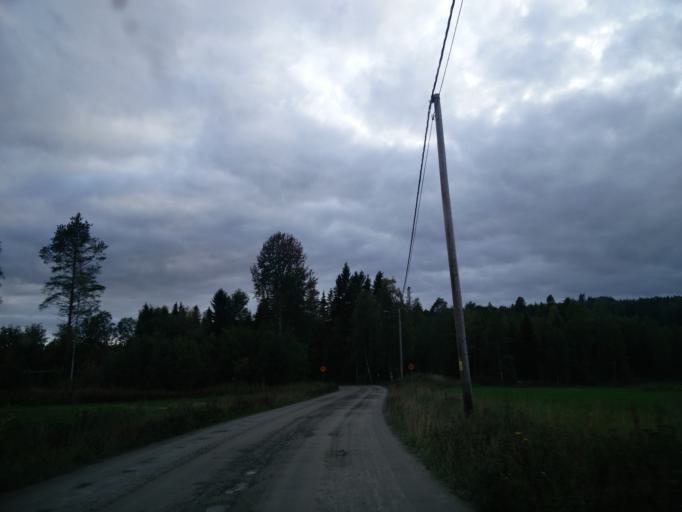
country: SE
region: Vaesternorrland
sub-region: Sundsvalls Kommun
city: Matfors
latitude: 62.3566
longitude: 17.0937
